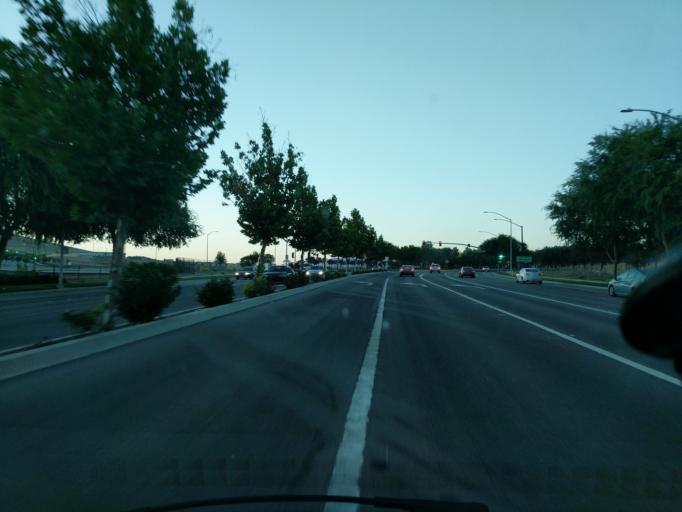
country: US
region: California
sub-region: Alameda County
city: Dublin
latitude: 37.7466
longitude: -121.9150
